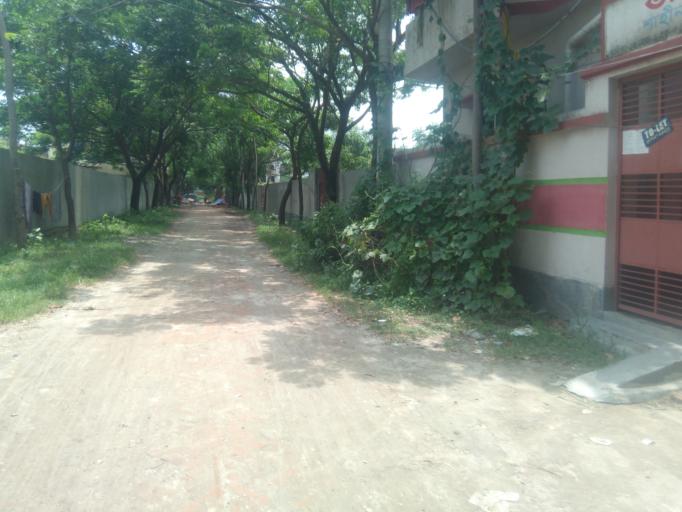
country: BD
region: Dhaka
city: Azimpur
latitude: 23.7520
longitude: 90.3467
